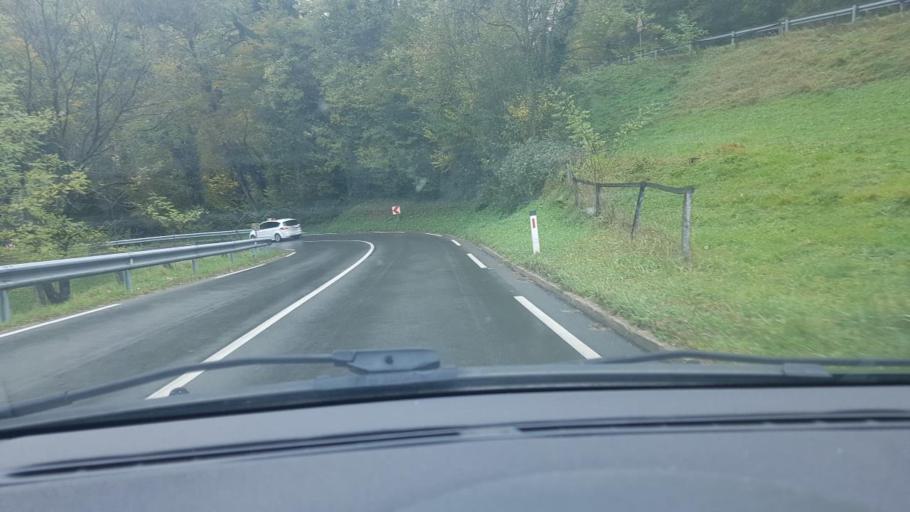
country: SI
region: Majsperk
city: Majsperk
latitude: 46.3528
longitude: 15.7376
